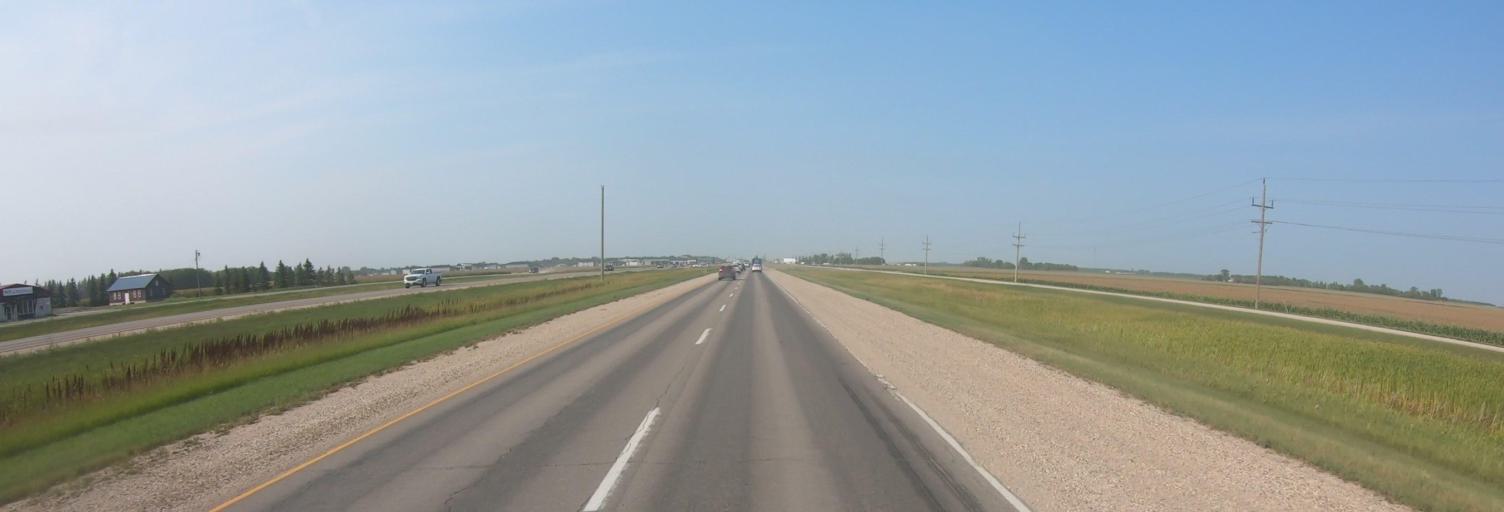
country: CA
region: Manitoba
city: Steinbach
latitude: 49.5869
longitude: -96.6875
